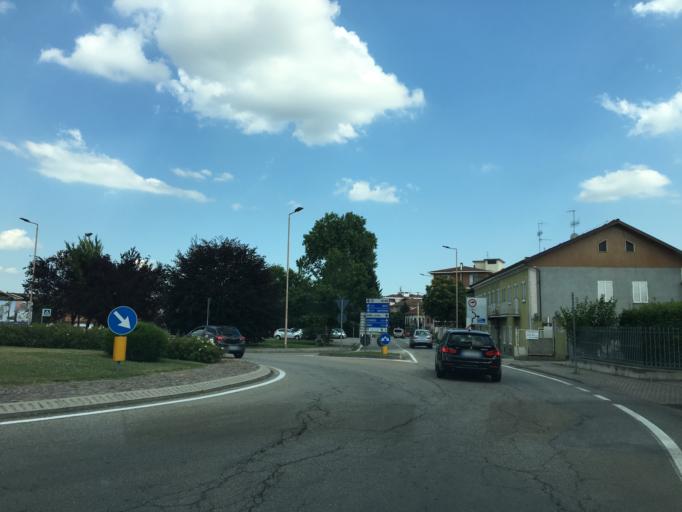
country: IT
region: Piedmont
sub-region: Provincia di Cuneo
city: Mussotto
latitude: 44.7141
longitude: 8.0154
